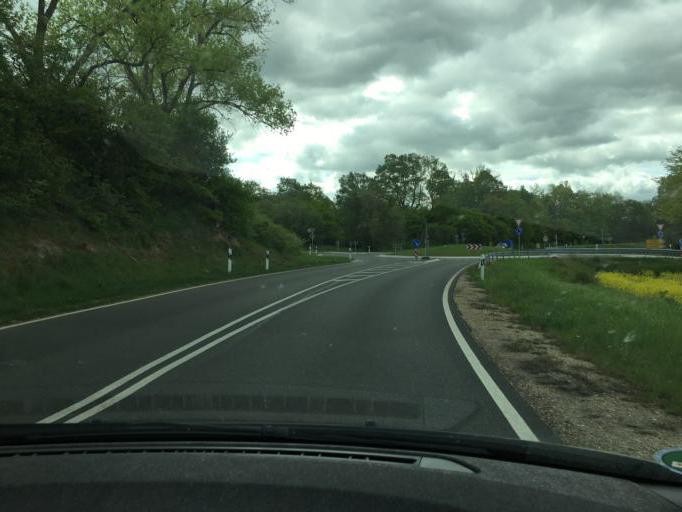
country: DE
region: North Rhine-Westphalia
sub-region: Regierungsbezirk Koln
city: Mechernich
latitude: 50.6422
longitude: 6.6557
